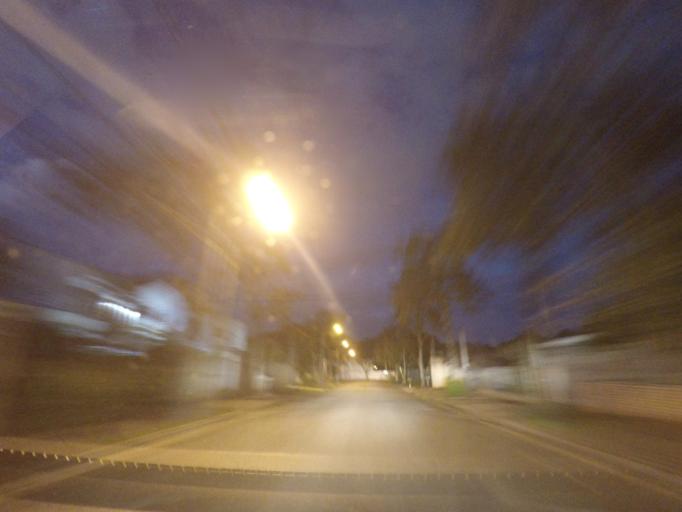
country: BR
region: Parana
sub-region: Curitiba
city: Curitiba
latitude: -25.4205
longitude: -49.2313
